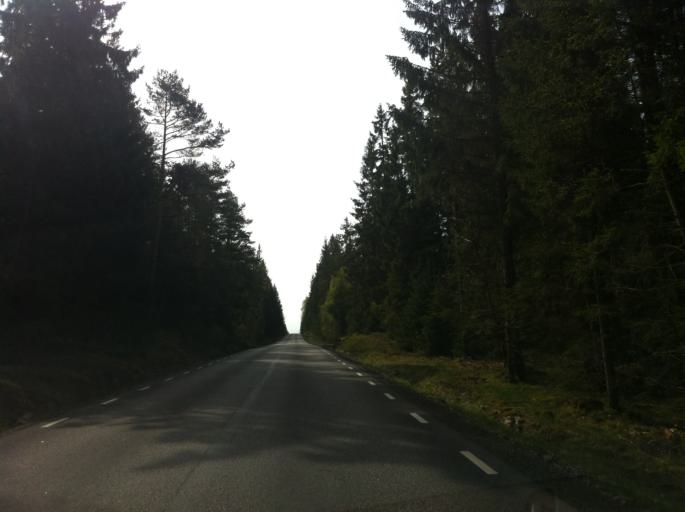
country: SE
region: Vaestra Goetaland
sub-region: Marks Kommun
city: Fritsla
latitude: 57.3900
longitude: 12.8540
